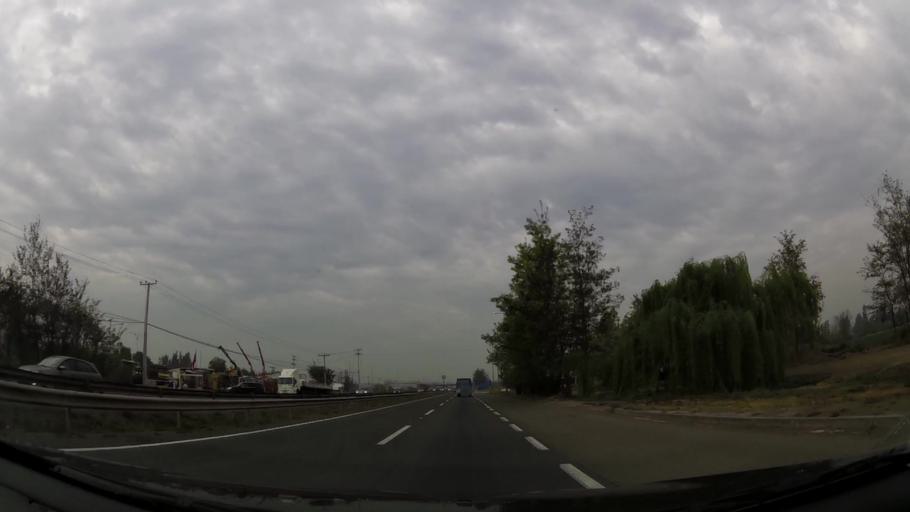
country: CL
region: Santiago Metropolitan
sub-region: Provincia de Chacabuco
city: Chicureo Abajo
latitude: -33.2309
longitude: -70.7610
